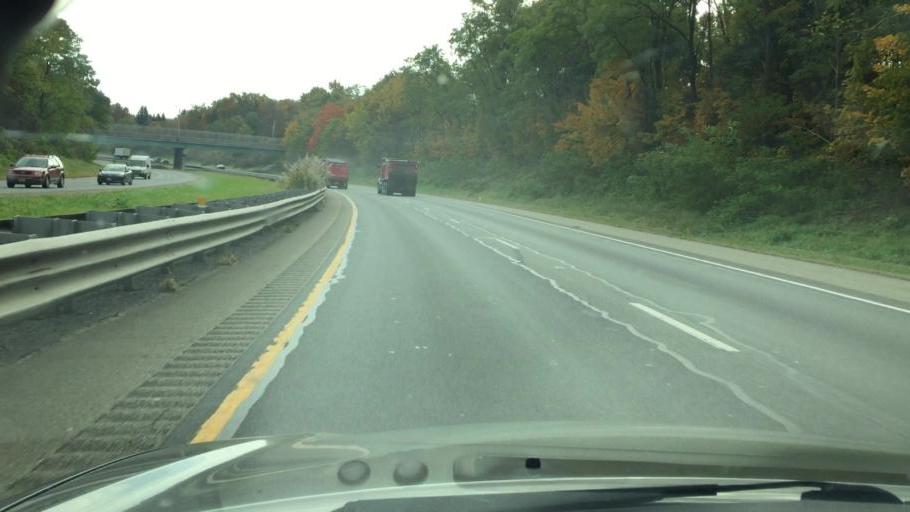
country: US
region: New Jersey
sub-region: Morris County
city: Madison
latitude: 40.7673
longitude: -74.4032
